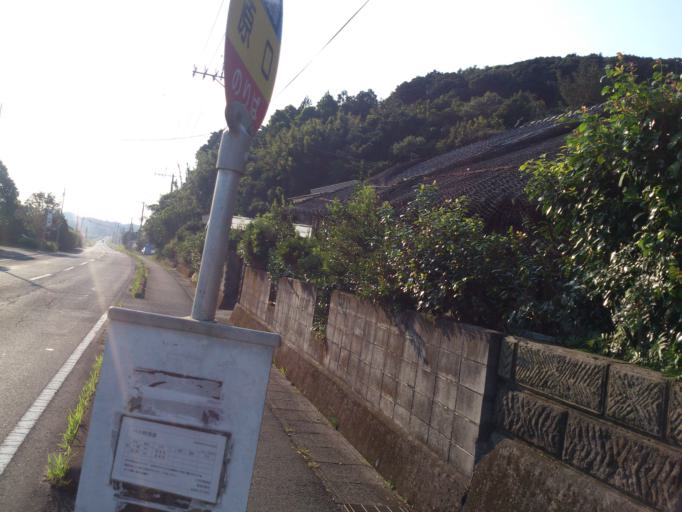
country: JP
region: Kagoshima
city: Kanoya
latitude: 31.3439
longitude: 130.9099
